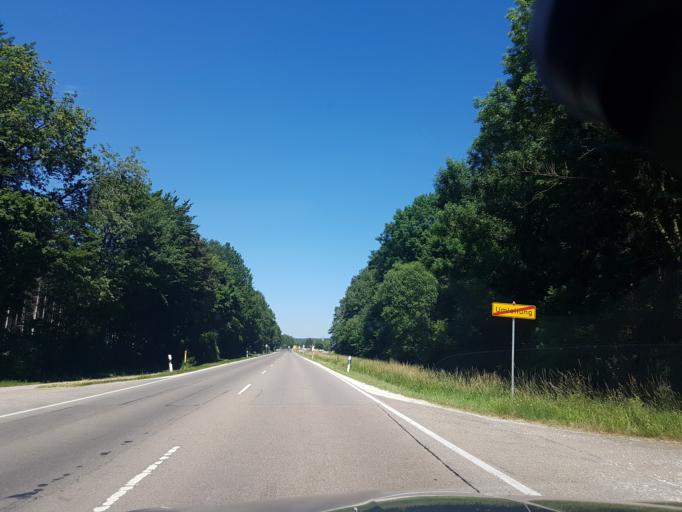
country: DE
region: Bavaria
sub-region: Swabia
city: Weissenhorn
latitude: 48.2908
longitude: 10.1331
